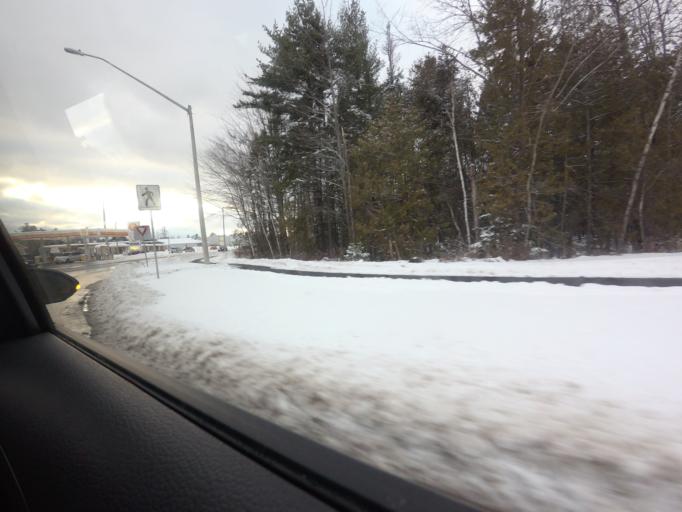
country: CA
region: New Brunswick
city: Oromocto
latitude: 45.8402
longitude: -66.4932
